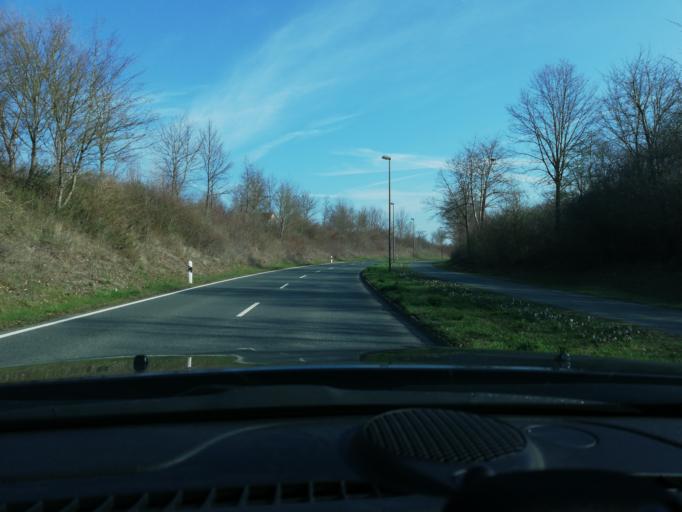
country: DE
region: Bavaria
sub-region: Regierungsbezirk Mittelfranken
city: Erlangen
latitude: 49.5978
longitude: 10.9552
